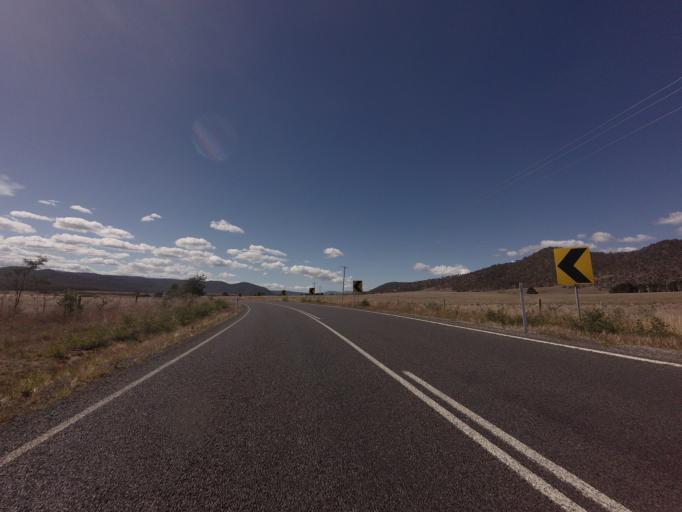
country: AU
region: Tasmania
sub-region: Break O'Day
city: St Helens
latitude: -41.7064
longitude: 147.8485
